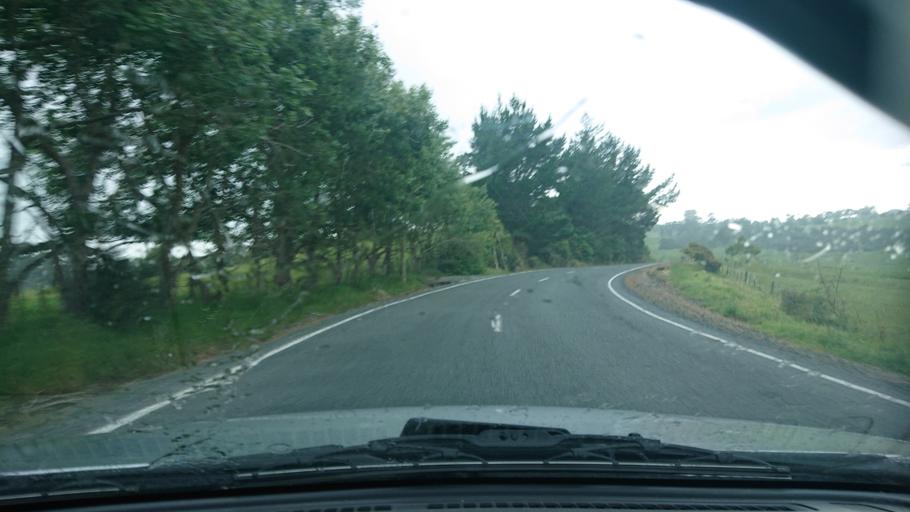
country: NZ
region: Auckland
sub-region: Auckland
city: Wellsford
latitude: -36.3315
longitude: 174.4020
